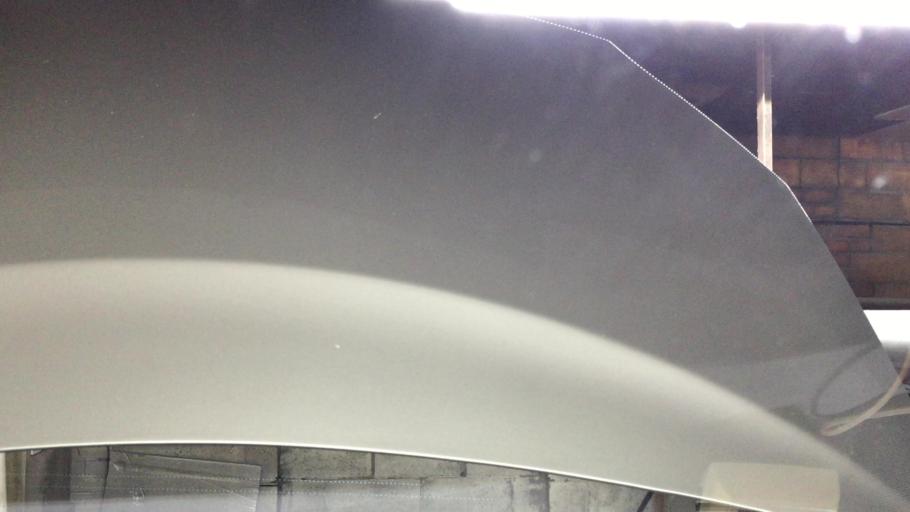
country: US
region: Pennsylvania
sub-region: Beaver County
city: Aliquippa
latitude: 40.6149
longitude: -80.2606
